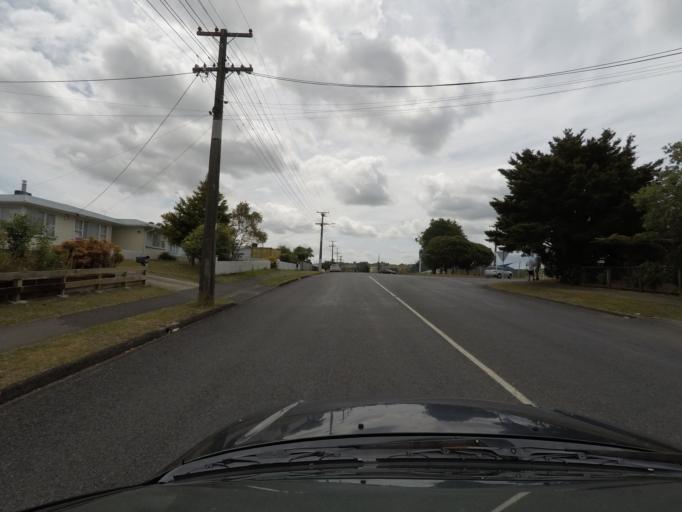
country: NZ
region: Northland
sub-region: Whangarei
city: Whangarei
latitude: -35.6814
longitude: 174.3253
